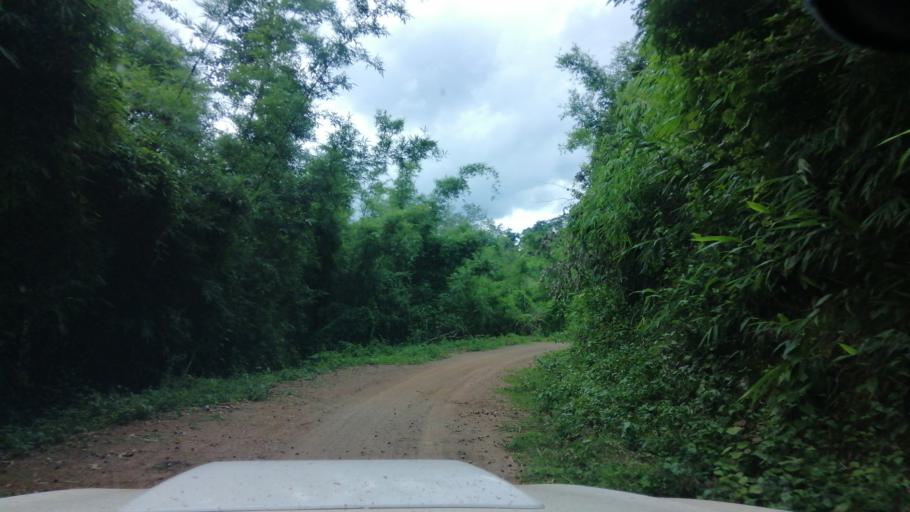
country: TH
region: Nan
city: Mae Charim
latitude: 18.7562
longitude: 101.2955
